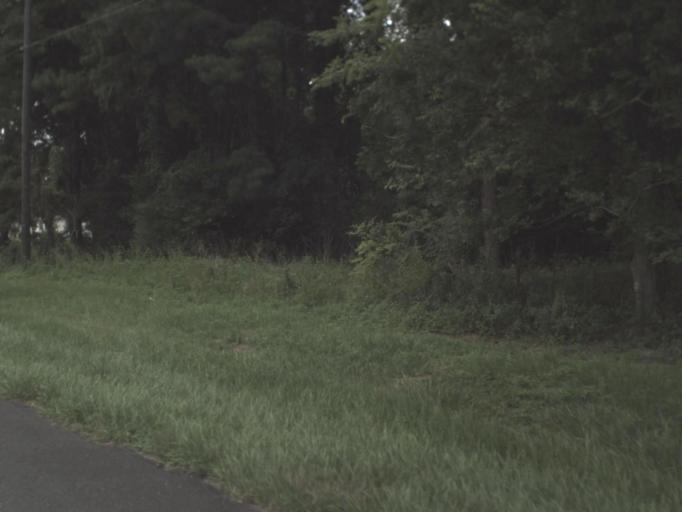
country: US
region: Florida
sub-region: Levy County
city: Williston
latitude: 29.4358
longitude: -82.4630
